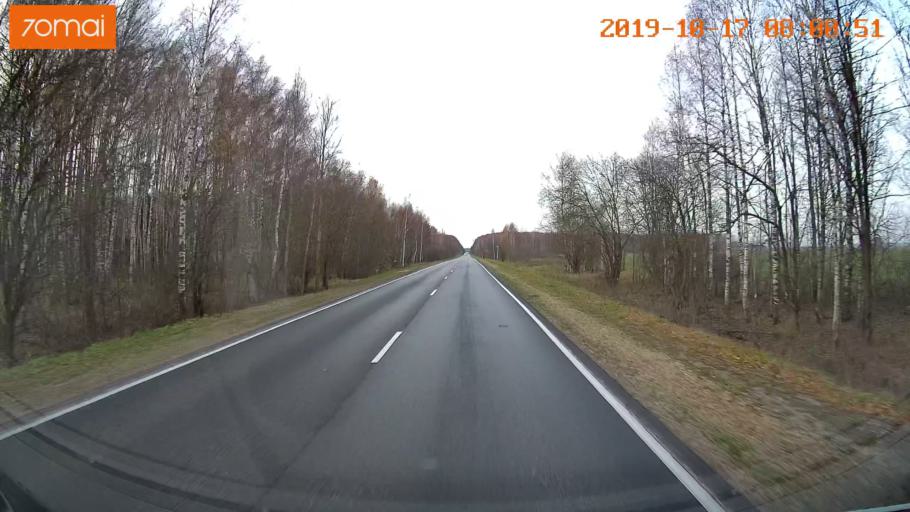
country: RU
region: Vladimir
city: Bavleny
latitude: 56.3791
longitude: 39.5091
